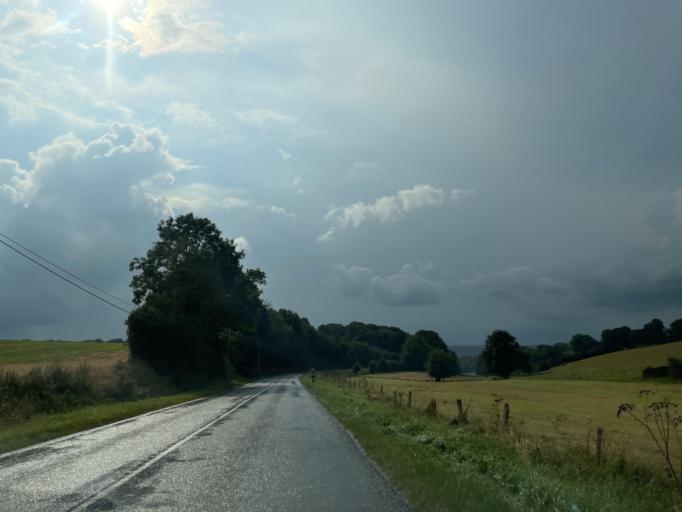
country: FR
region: Haute-Normandie
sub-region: Departement de la Seine-Maritime
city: Envermeu
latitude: 49.9091
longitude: 1.2757
